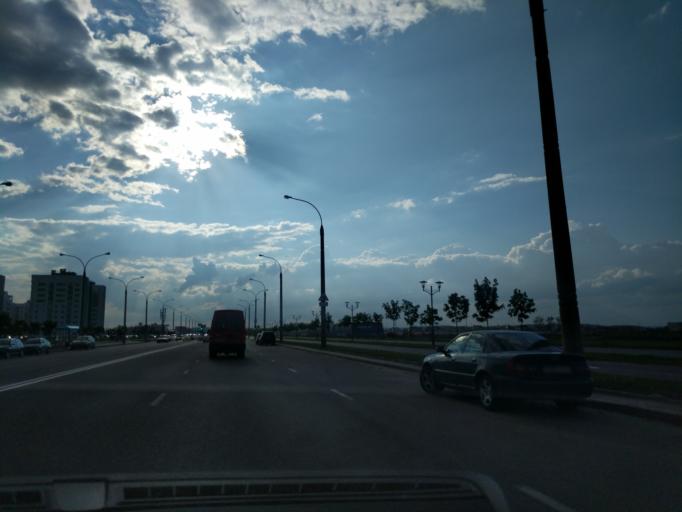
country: BY
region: Minsk
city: Zhdanovichy
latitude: 53.9168
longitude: 27.4238
